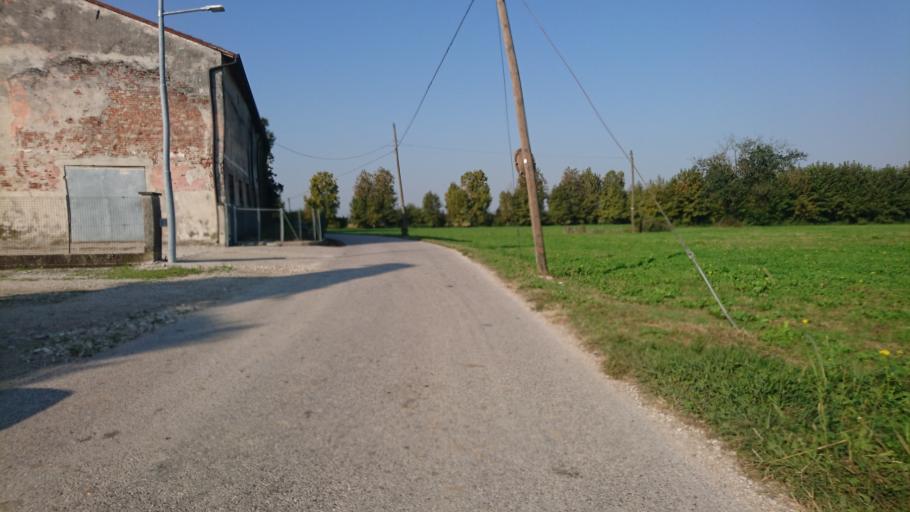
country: IT
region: Veneto
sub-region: Provincia di Padova
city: Gazzo
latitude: 45.6021
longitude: 11.7067
